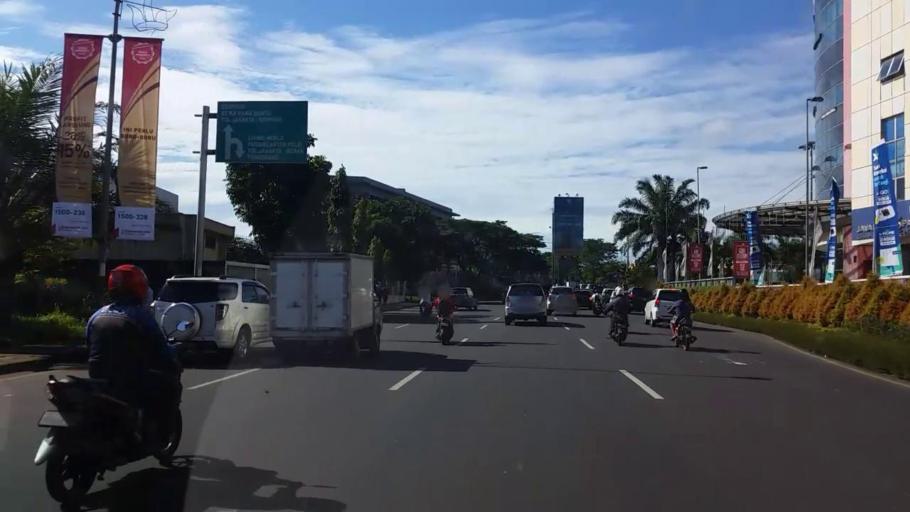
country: ID
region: West Java
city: Serpong
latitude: -6.2855
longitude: 106.6657
